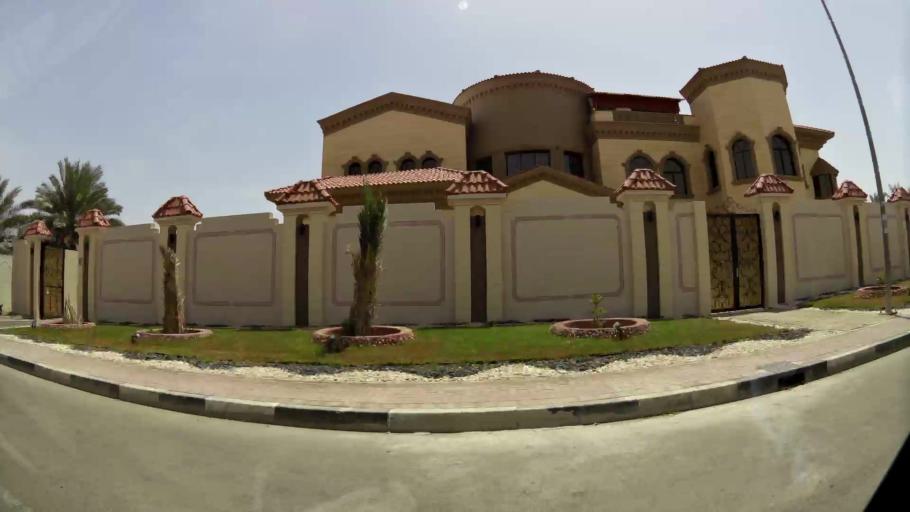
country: AE
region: Abu Dhabi
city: Al Ain
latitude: 24.1788
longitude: 55.7242
